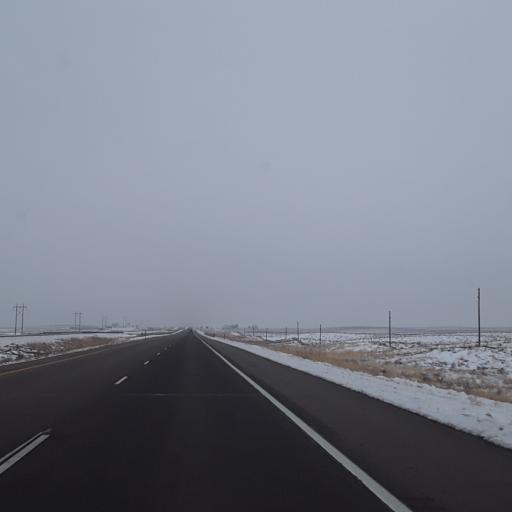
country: US
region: Colorado
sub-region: Logan County
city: Sterling
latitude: 40.4862
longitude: -103.2737
